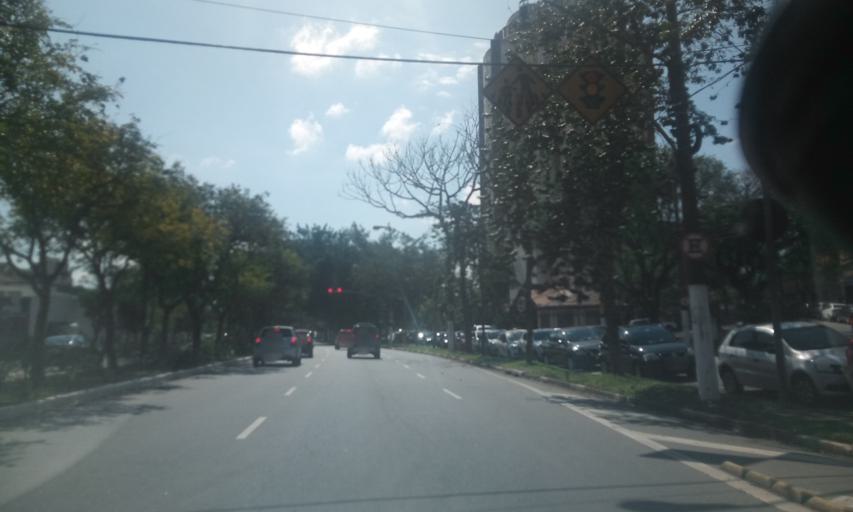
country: BR
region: Sao Paulo
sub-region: Sao Bernardo Do Campo
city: Sao Bernardo do Campo
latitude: -23.6927
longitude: -46.5605
